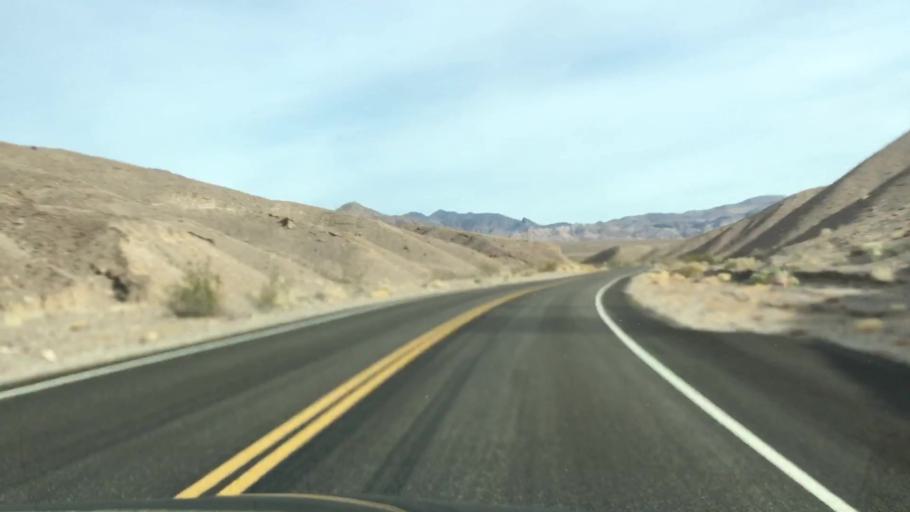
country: US
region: Nevada
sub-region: Nye County
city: Beatty
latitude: 36.6758
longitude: -117.0111
